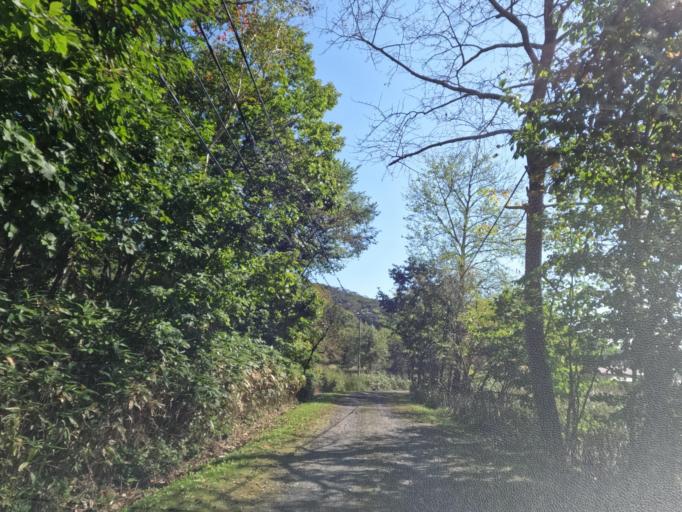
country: JP
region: Hokkaido
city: Muroran
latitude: 42.3917
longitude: 141.0303
